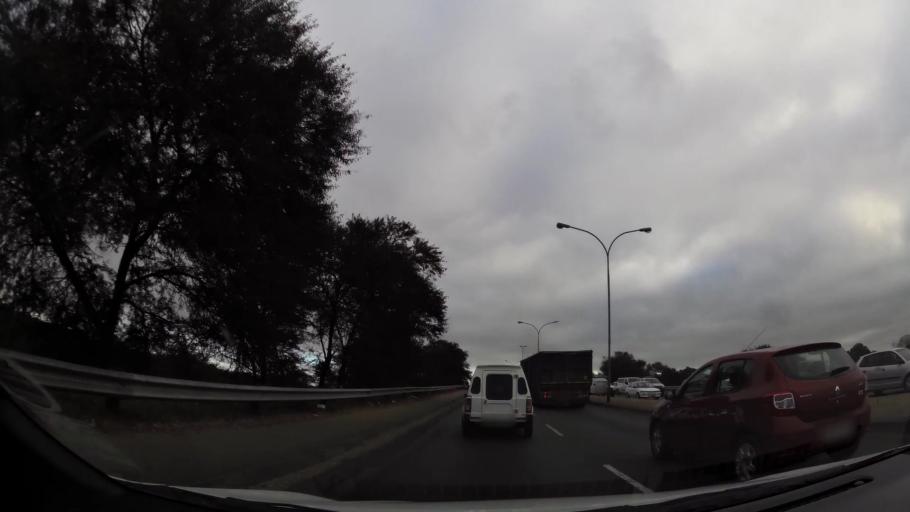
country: ZA
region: Limpopo
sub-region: Capricorn District Municipality
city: Polokwane
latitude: -23.9033
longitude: 29.4411
